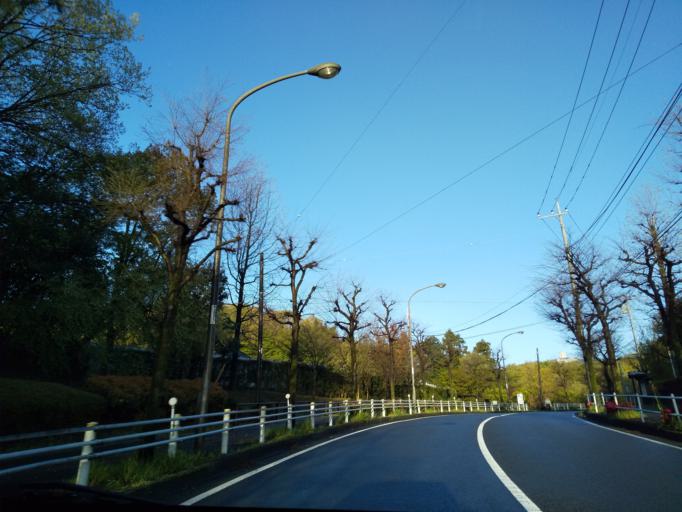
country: JP
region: Tokyo
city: Hachioji
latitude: 35.6074
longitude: 139.3687
